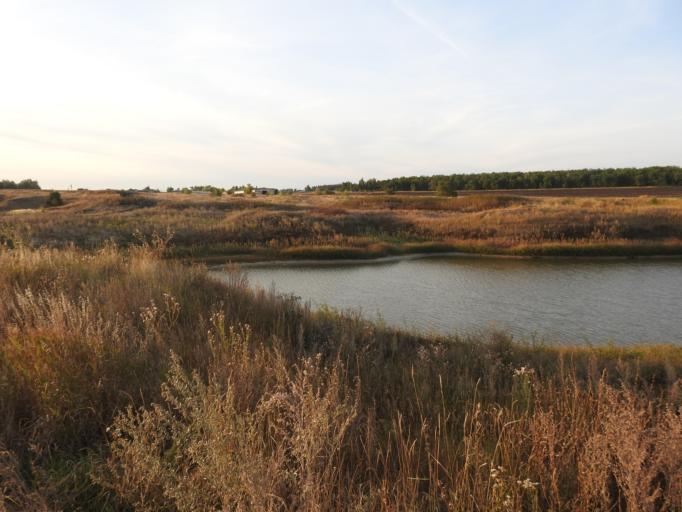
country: RU
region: Saratov
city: Novyye Burasy
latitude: 52.1918
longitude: 46.1038
